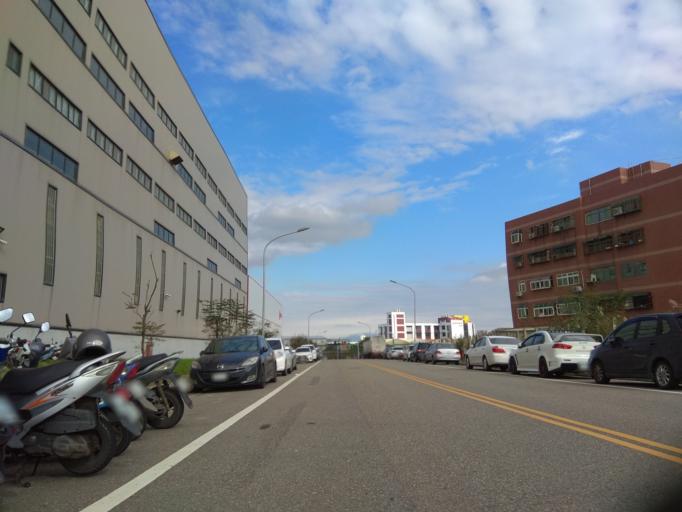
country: TW
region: Taiwan
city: Taoyuan City
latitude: 25.0588
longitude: 121.1773
